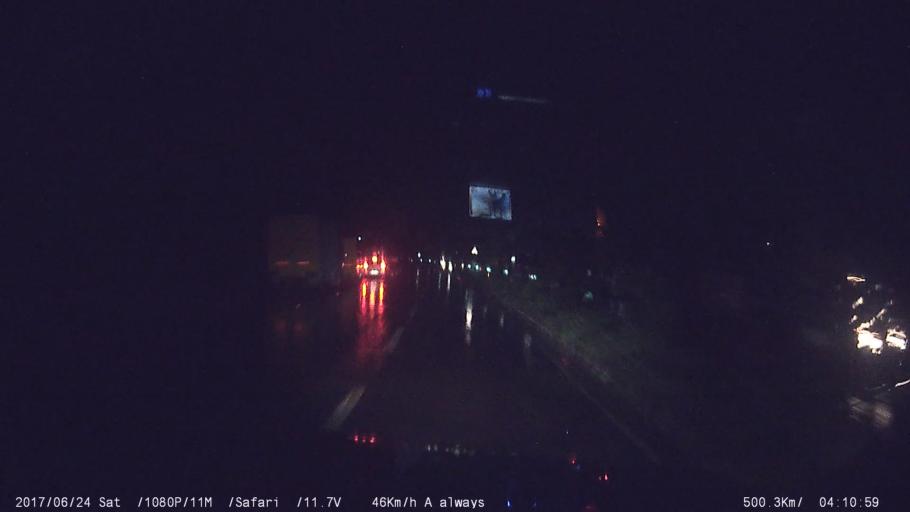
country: IN
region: Kerala
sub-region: Ernakulam
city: Elur
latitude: 10.0548
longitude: 76.3248
